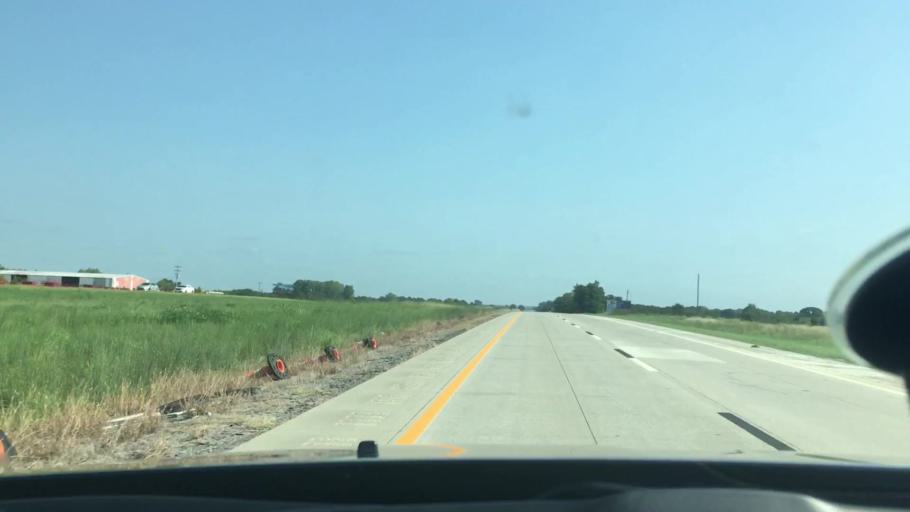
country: US
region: Oklahoma
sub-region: Atoka County
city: Atoka
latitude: 34.1947
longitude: -96.2408
